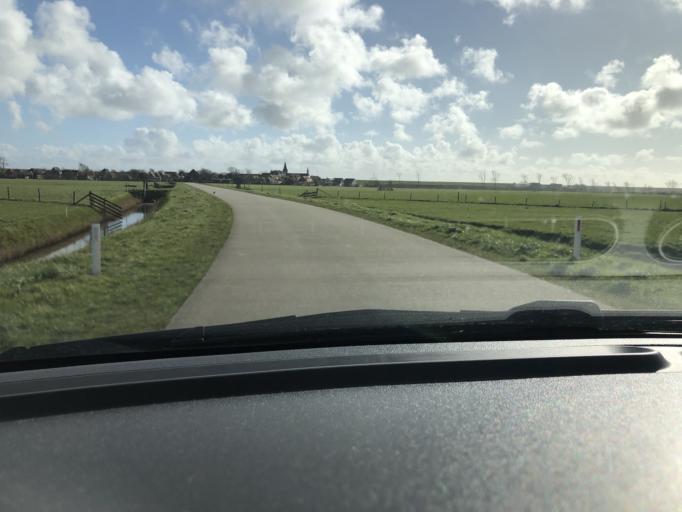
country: NL
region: North Holland
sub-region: Gemeente Texel
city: Den Burg
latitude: 53.0376
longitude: 4.8407
